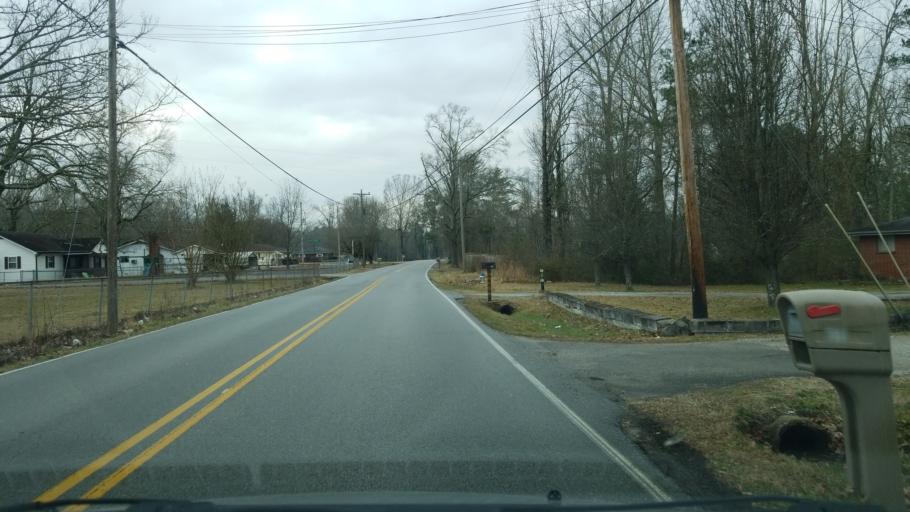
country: US
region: Georgia
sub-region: Catoosa County
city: Indian Springs
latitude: 34.9658
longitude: -85.1589
